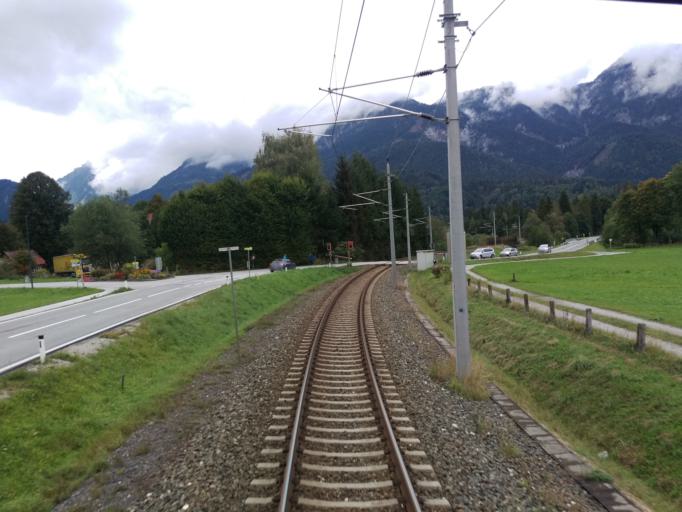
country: AT
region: Styria
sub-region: Politischer Bezirk Liezen
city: Aich
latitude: 47.4180
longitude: 13.7949
